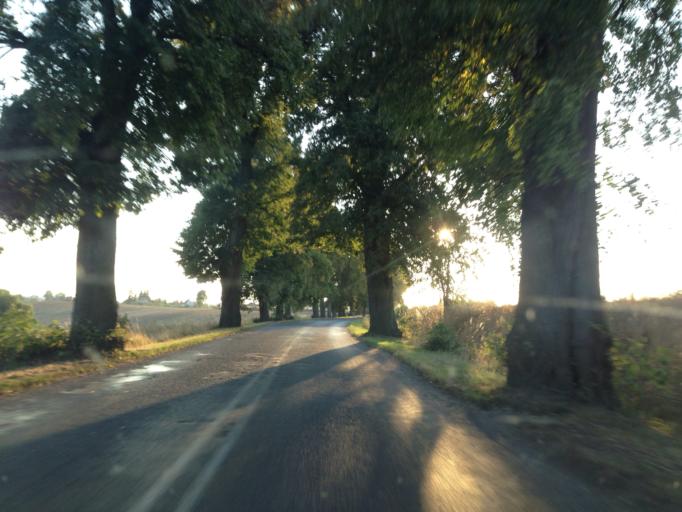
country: PL
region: Pomeranian Voivodeship
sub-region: Powiat sztumski
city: Dzierzgon
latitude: 53.9307
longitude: 19.3308
